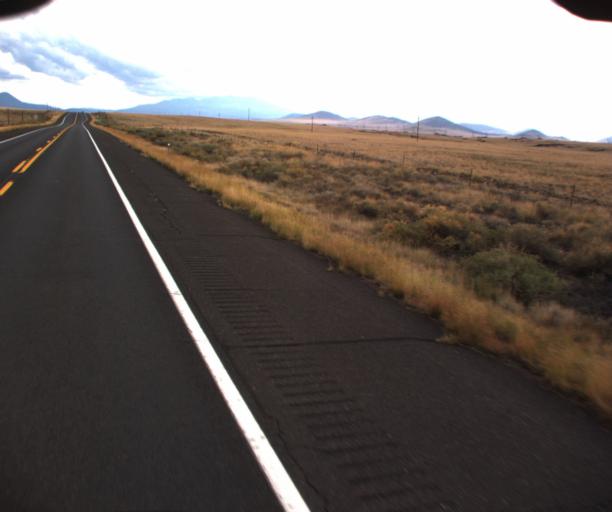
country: US
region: Arizona
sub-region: Coconino County
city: Flagstaff
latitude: 35.6397
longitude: -111.5183
